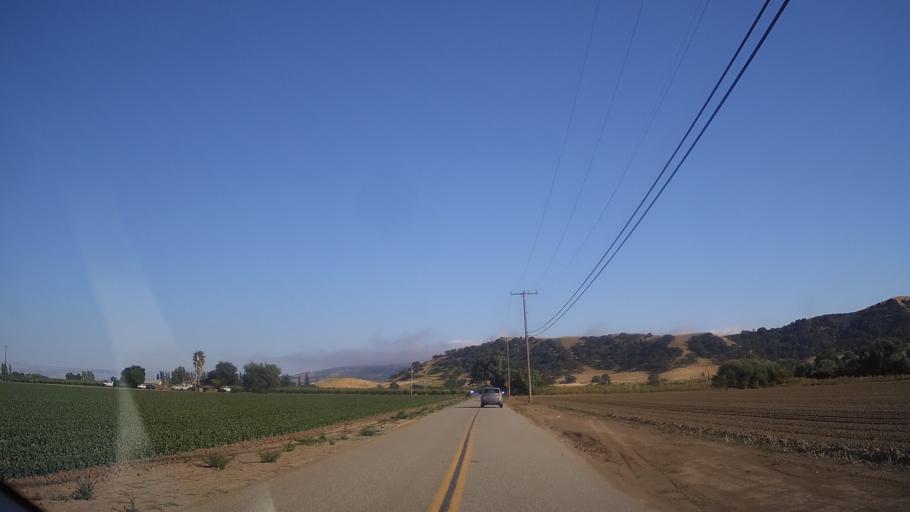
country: US
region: California
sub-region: Santa Clara County
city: Gilroy
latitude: 36.9756
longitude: -121.5640
